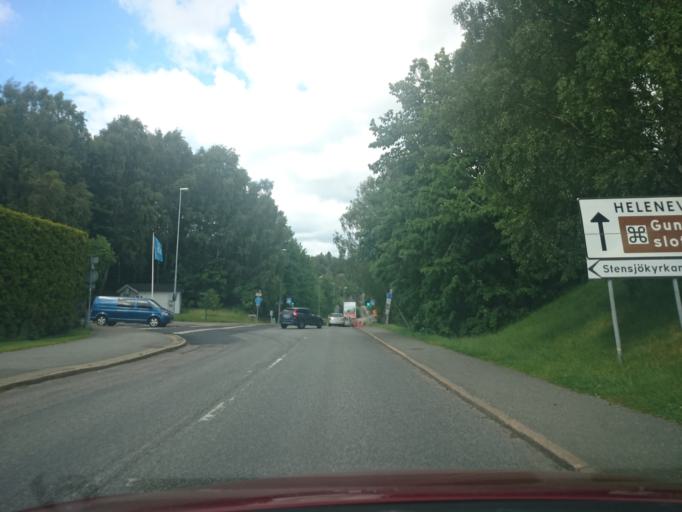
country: SE
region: Vaestra Goetaland
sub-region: Molndal
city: Moelndal
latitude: 57.6621
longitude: 12.0389
